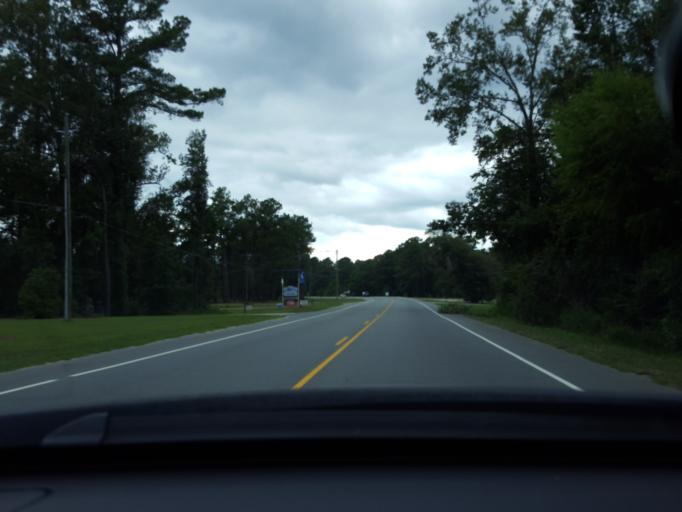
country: US
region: North Carolina
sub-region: Bladen County
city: Elizabethtown
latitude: 34.6569
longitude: -78.5045
